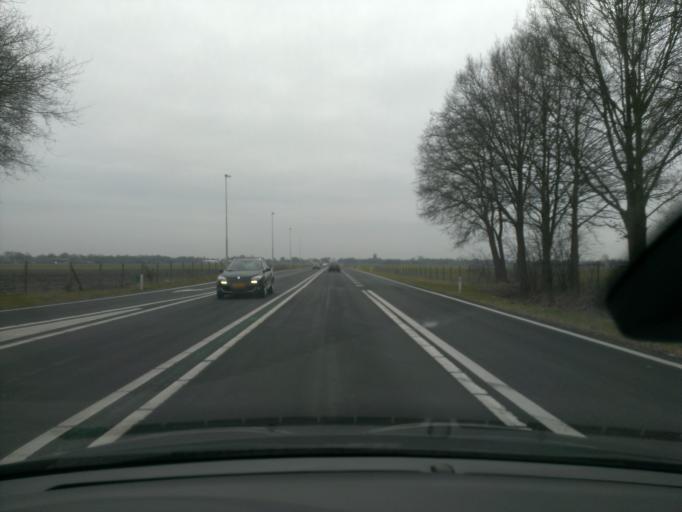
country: NL
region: Overijssel
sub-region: Gemeente Twenterand
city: Westerhaar-Vriezenveensewijk
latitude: 52.4325
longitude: 6.6296
